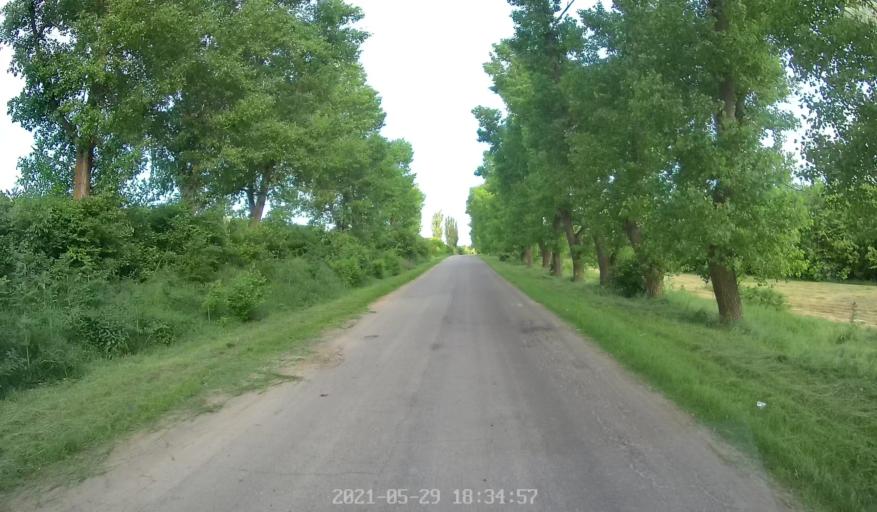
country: MD
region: Chisinau
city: Singera
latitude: 46.8108
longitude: 28.9166
